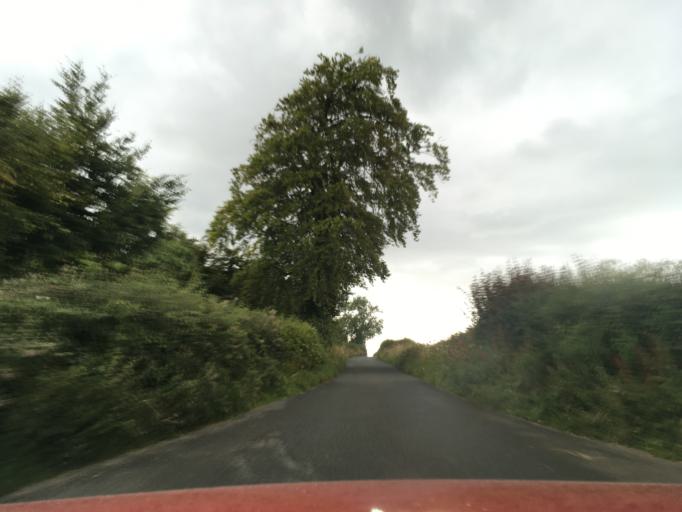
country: GB
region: England
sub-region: Gloucestershire
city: Shurdington
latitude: 51.8089
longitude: -2.1289
